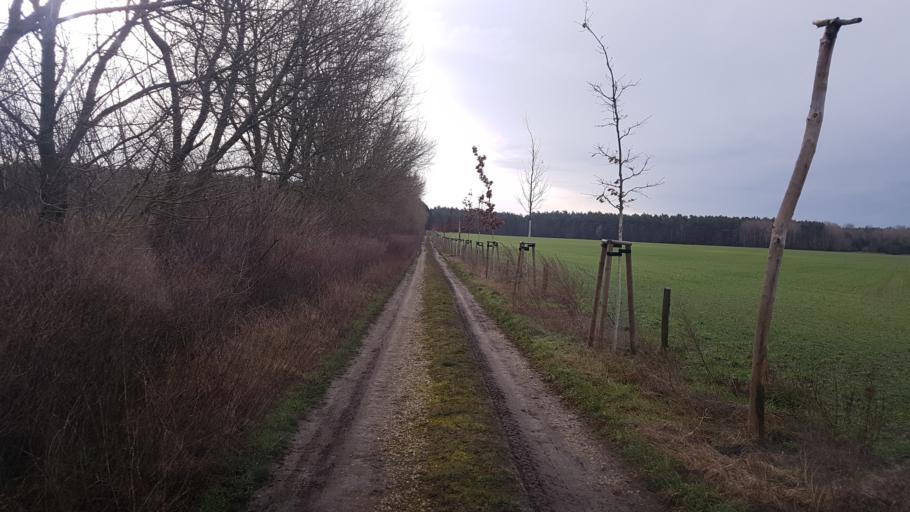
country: DE
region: Brandenburg
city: Sallgast
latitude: 51.6142
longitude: 13.8123
